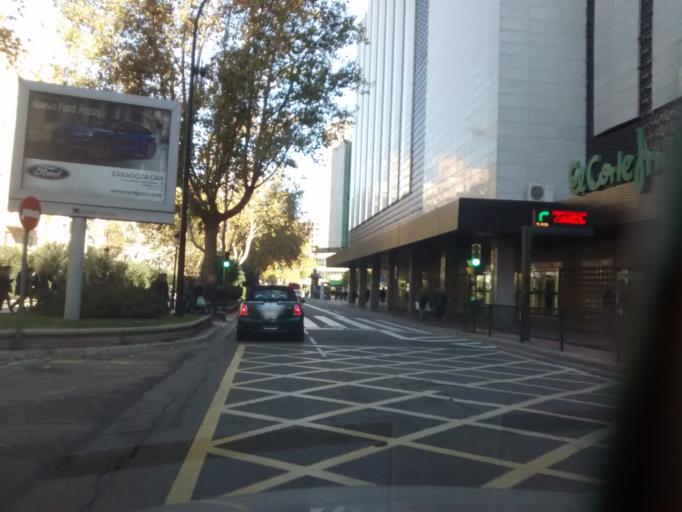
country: ES
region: Aragon
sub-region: Provincia de Zaragoza
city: Zaragoza
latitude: 41.6448
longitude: -0.8858
